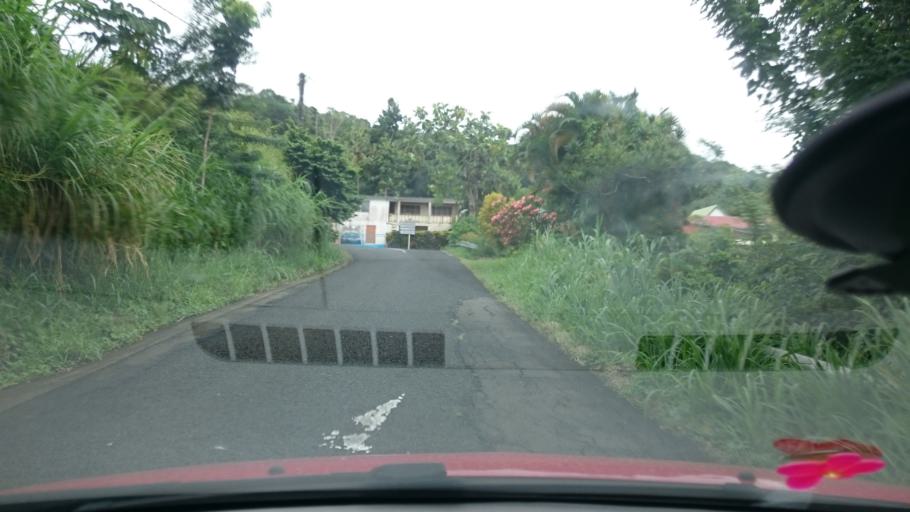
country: MQ
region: Martinique
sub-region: Martinique
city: Riviere-Pilote
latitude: 14.4951
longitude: -60.9239
